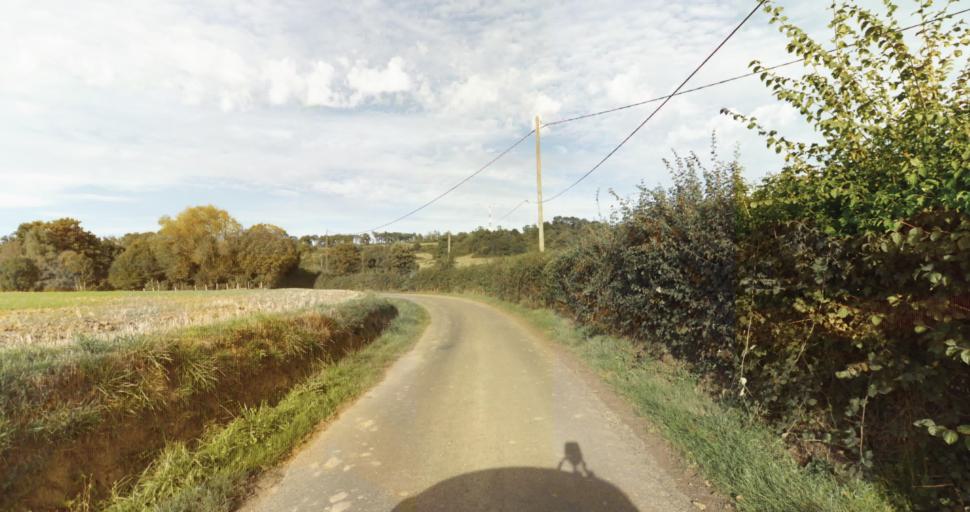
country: FR
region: Lower Normandy
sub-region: Departement de l'Orne
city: Gace
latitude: 48.7133
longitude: 0.3111
